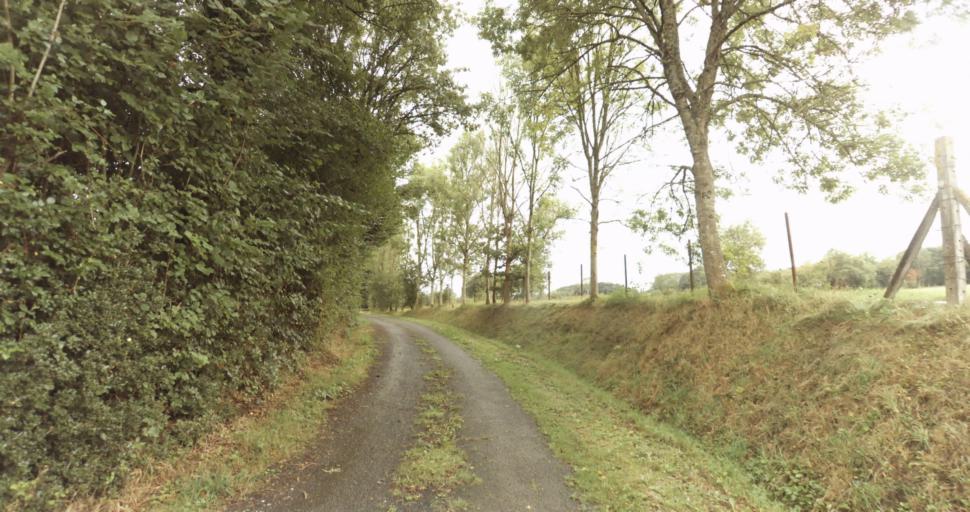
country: FR
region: Lower Normandy
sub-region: Departement de l'Orne
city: Sainte-Gauburge-Sainte-Colombe
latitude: 48.7067
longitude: 0.4279
